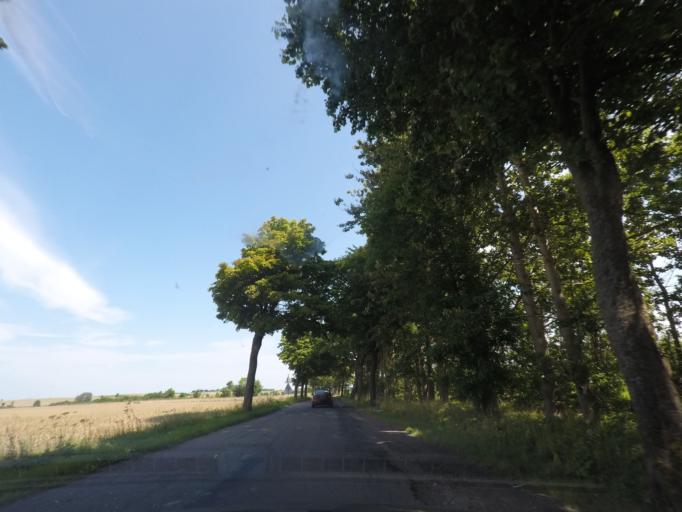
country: PL
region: West Pomeranian Voivodeship
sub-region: Powiat slawienski
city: Darlowo
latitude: 54.4383
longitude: 16.4407
